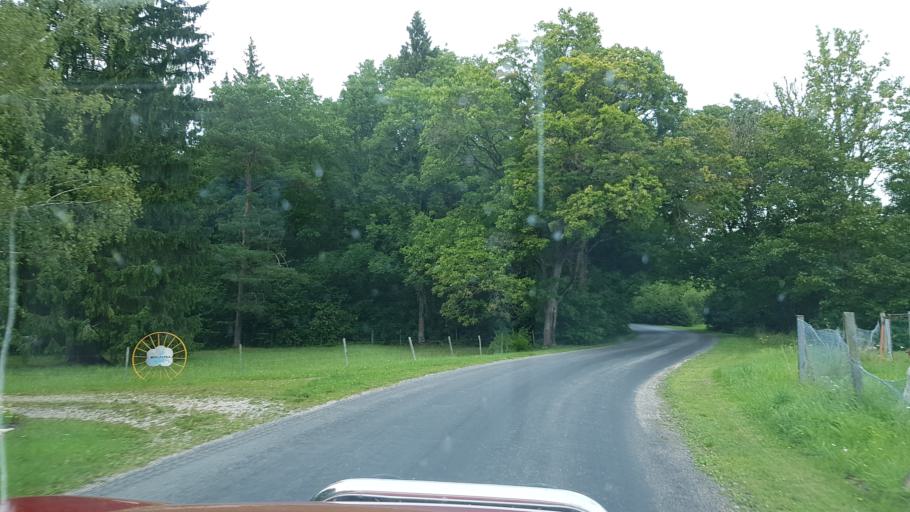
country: EE
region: Laeaene
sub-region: Ridala Parish
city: Uuemoisa
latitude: 59.0030
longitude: 23.7214
